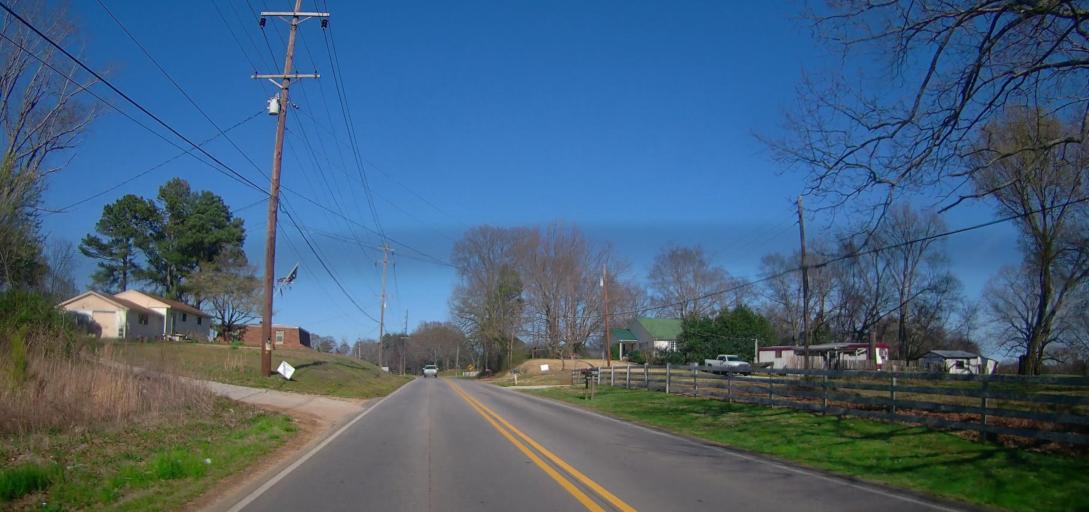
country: US
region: Alabama
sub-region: Lauderdale County
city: East Florence
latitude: 34.8296
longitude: -87.6174
